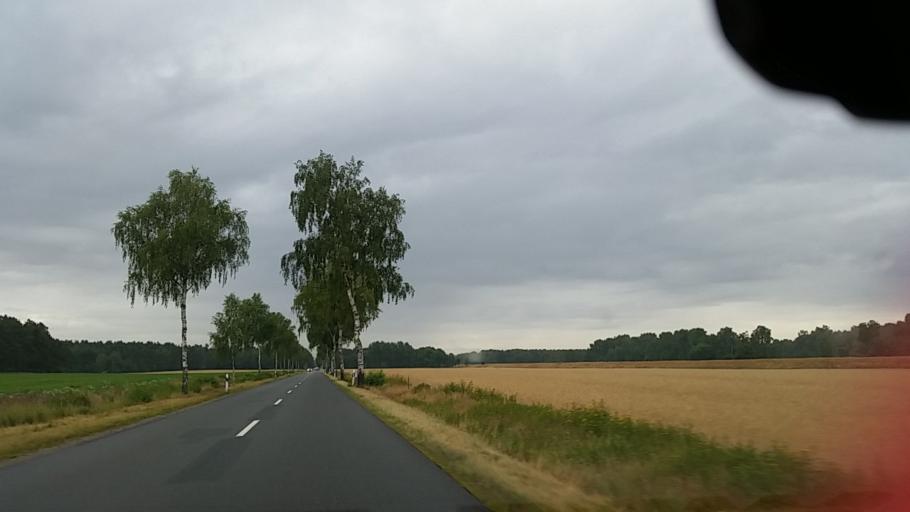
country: DE
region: Lower Saxony
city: Schoneworde
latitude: 52.5891
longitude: 10.6805
